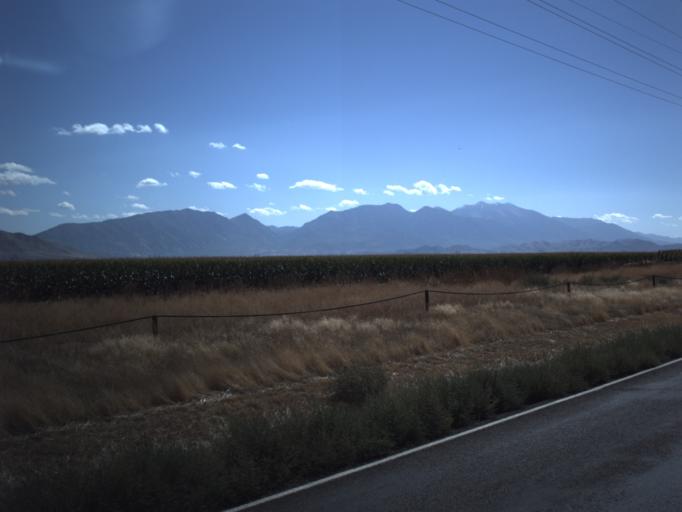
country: US
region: Utah
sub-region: Utah County
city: Genola
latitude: 40.1072
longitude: -111.9592
